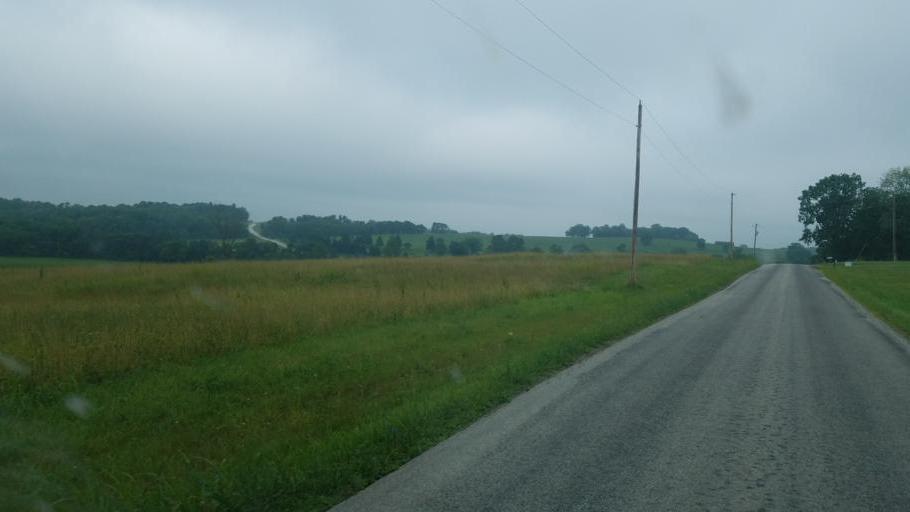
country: US
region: Ohio
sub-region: Highland County
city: Hillsboro
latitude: 39.2495
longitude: -83.5569
